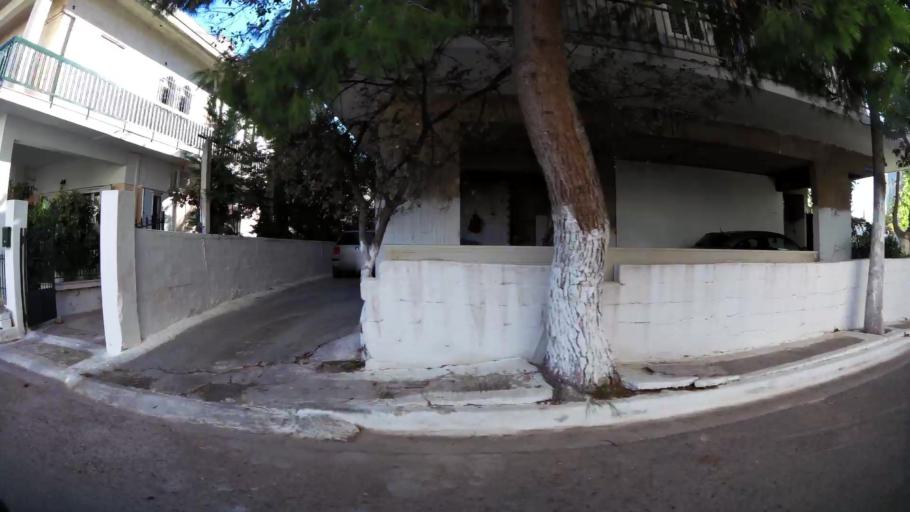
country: GR
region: Attica
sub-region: Nomarchia Anatolikis Attikis
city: Koropi
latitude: 37.9006
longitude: 23.8643
